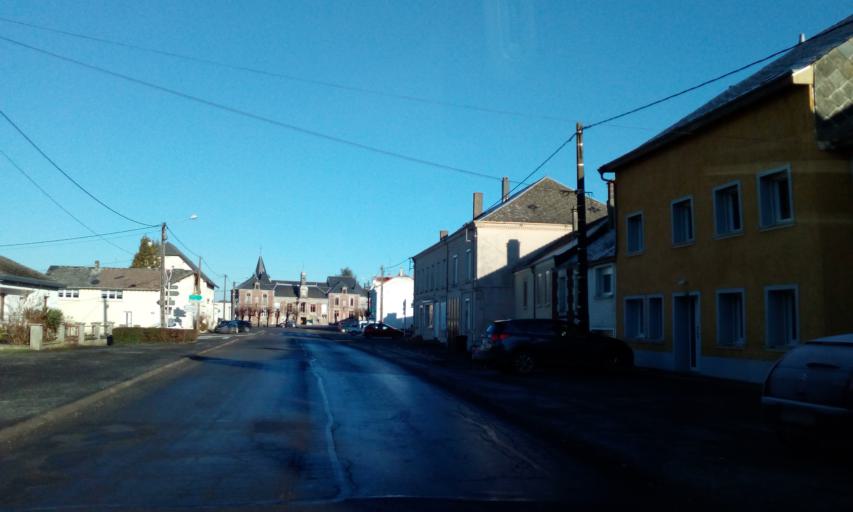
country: FR
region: Champagne-Ardenne
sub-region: Departement des Ardennes
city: Signy-le-Petit
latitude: 49.7674
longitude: 4.3397
